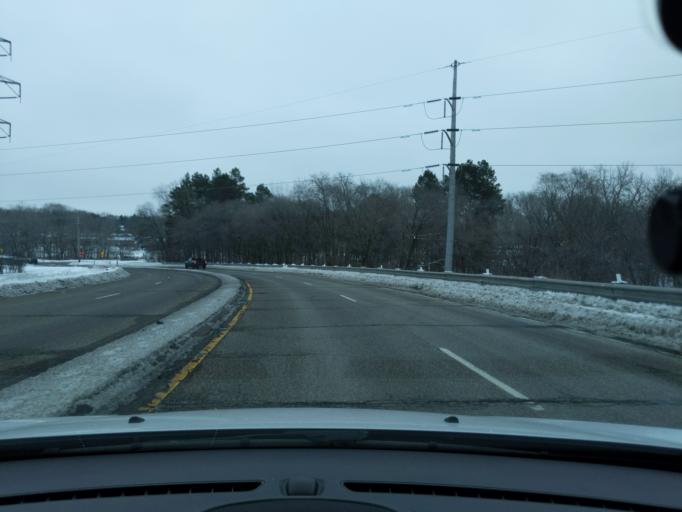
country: US
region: Minnesota
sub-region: Ramsey County
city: Roseville
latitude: 45.0197
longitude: -93.1402
